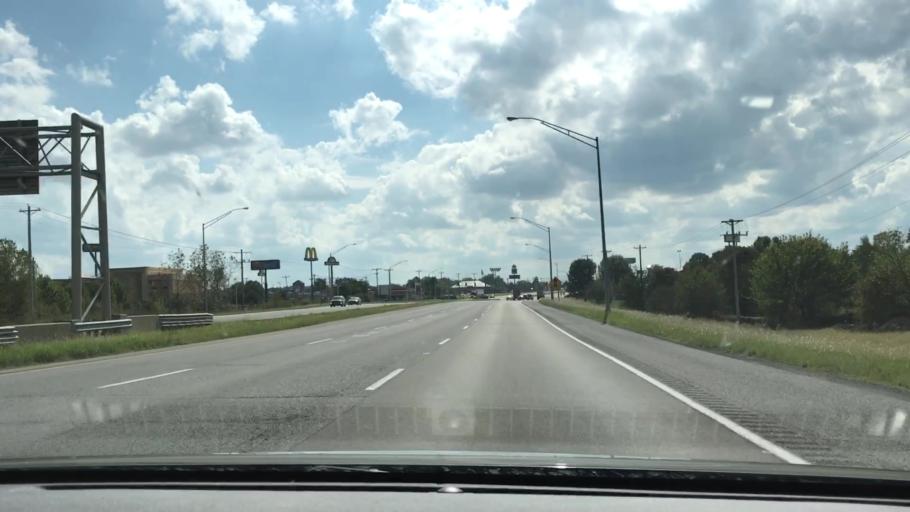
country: US
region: Kentucky
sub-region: Christian County
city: Oak Grove
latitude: 36.6994
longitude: -87.4542
